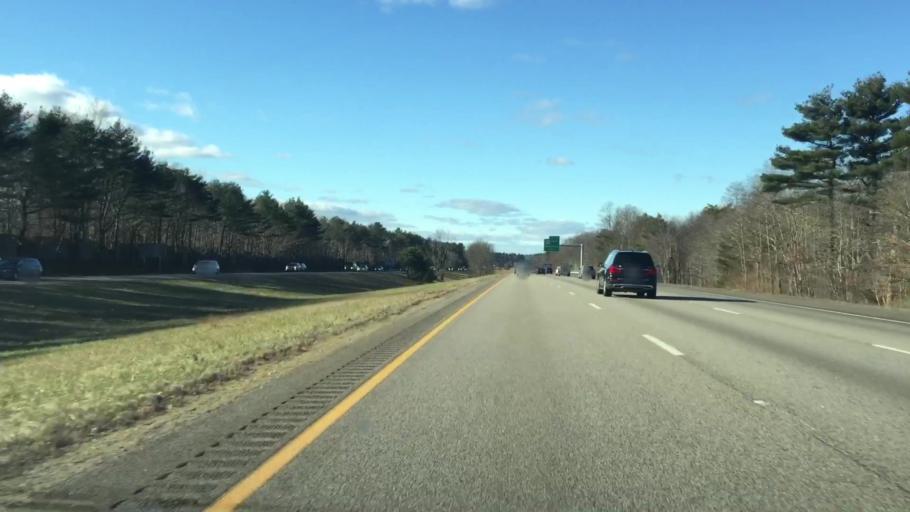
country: US
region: Massachusetts
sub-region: Bristol County
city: Norton Center
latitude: 41.9967
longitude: -71.1942
